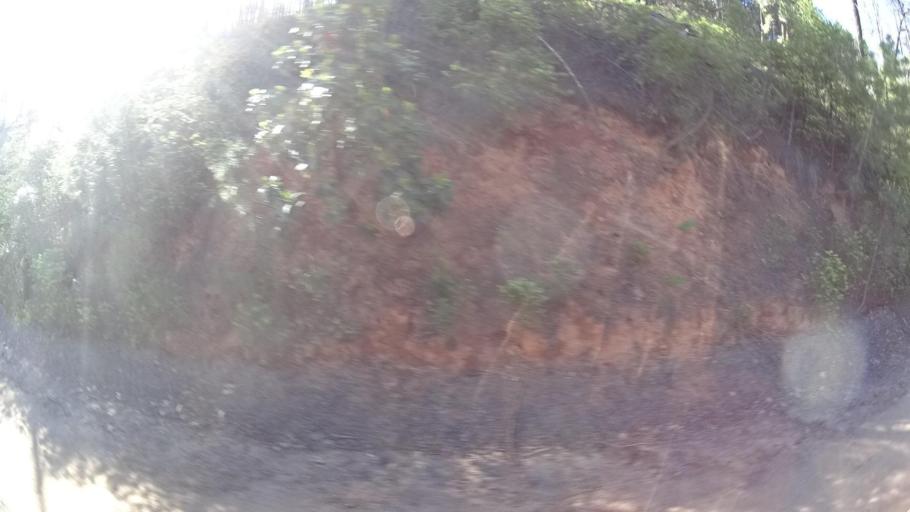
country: US
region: California
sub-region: Lake County
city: Upper Lake
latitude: 39.3792
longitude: -122.9888
